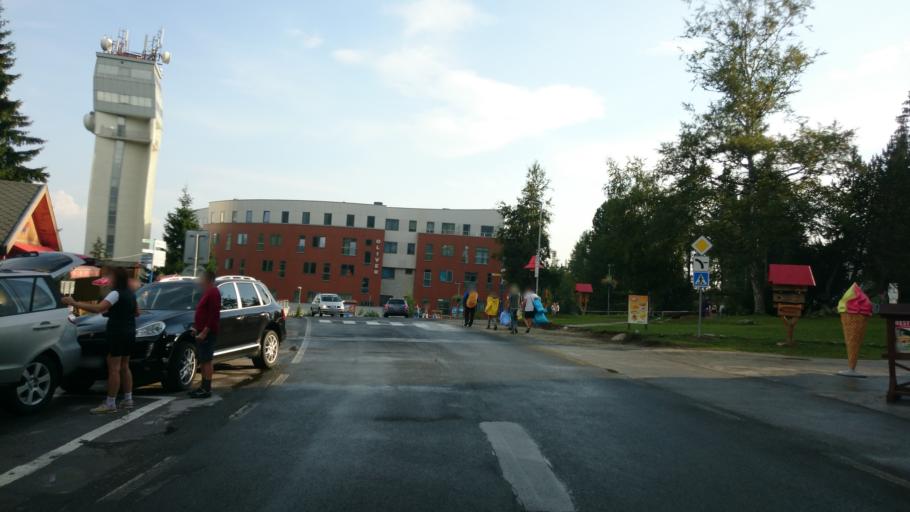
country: SK
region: Presovsky
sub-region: Okres Poprad
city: Strba
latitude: 49.1212
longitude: 20.0633
